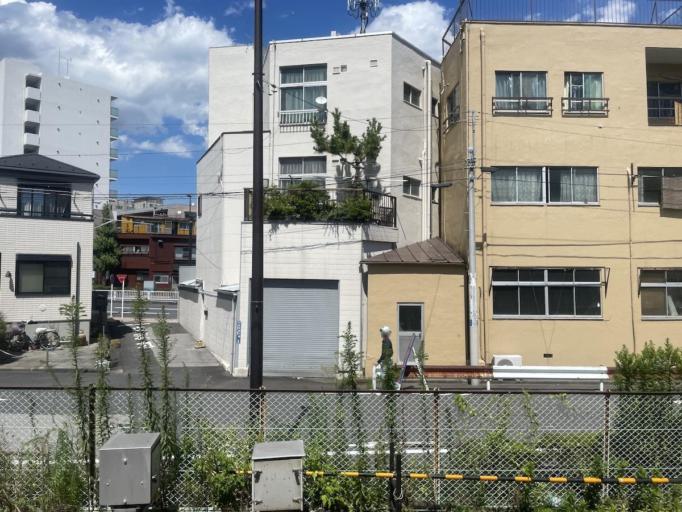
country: JP
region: Tokyo
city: Urayasu
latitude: 35.7090
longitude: 139.8304
